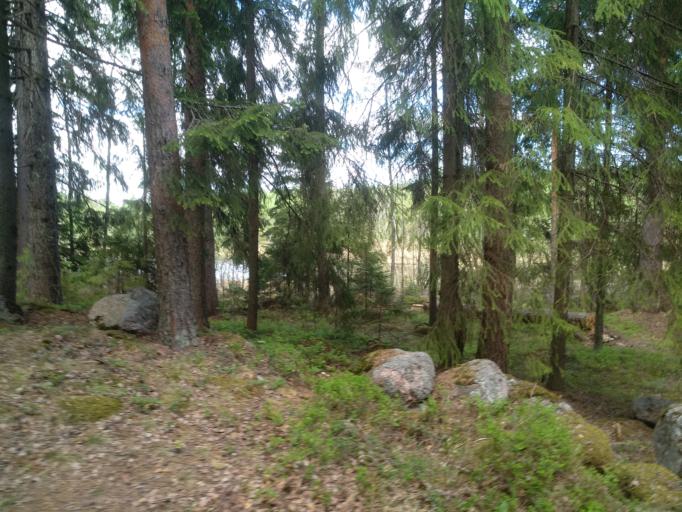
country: RU
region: Leningrad
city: Veshchevo
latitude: 60.7549
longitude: 29.1166
